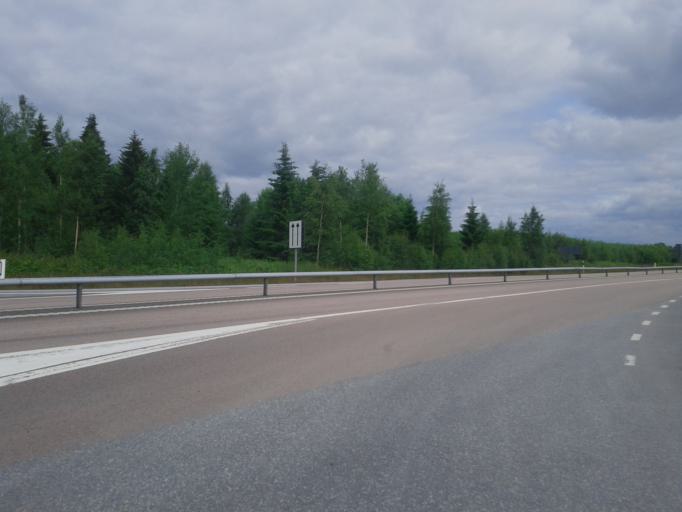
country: SE
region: Vaesternorrland
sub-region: OErnskoeldsviks Kommun
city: Bjasta
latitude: 63.2079
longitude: 18.4880
